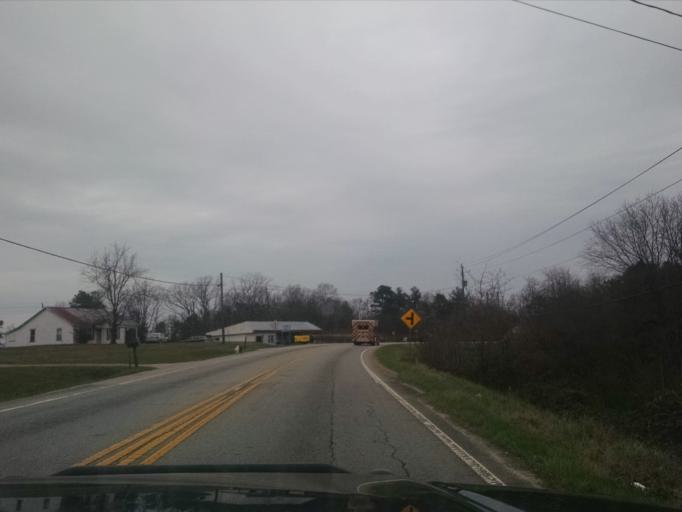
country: US
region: Georgia
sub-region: Hall County
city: Oakwood
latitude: 34.2139
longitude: -83.8787
